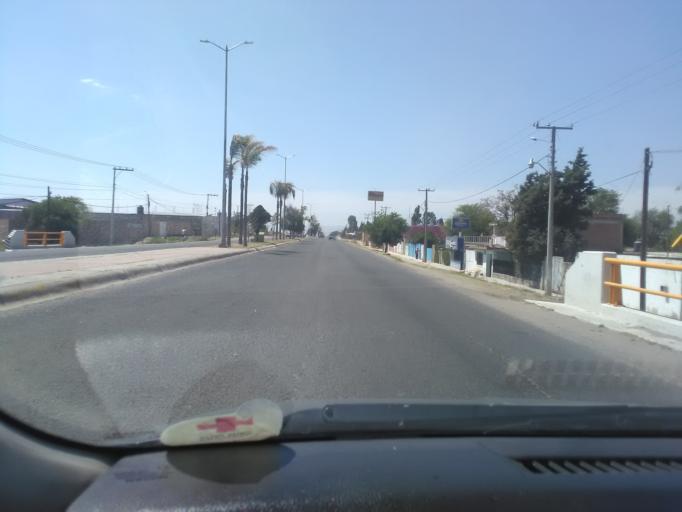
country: MX
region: Durango
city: Victoria de Durango
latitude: 24.0268
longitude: -104.5786
